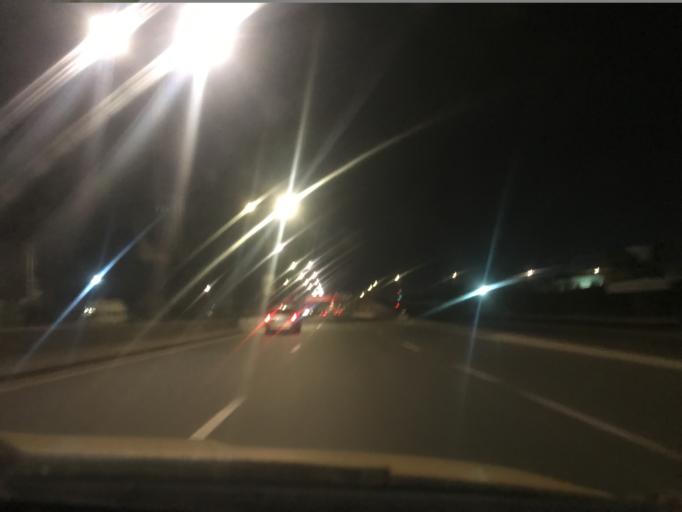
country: SN
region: Dakar
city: Dakar
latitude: 14.6954
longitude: -17.4424
